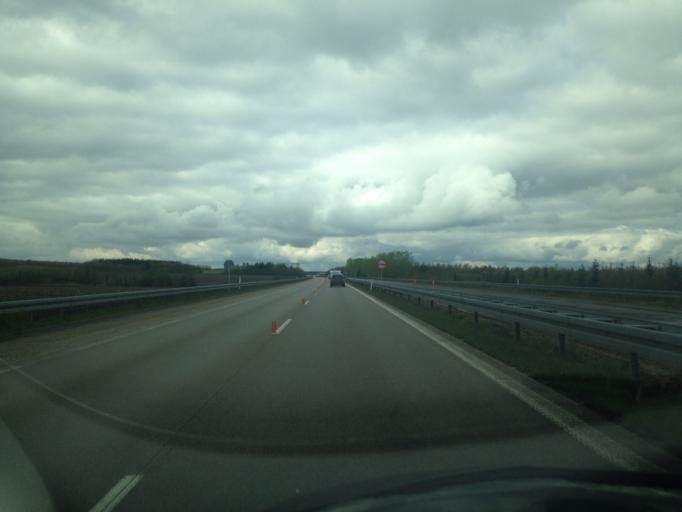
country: DK
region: South Denmark
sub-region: Vejen Kommune
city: Holsted
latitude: 55.5211
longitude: 8.8756
